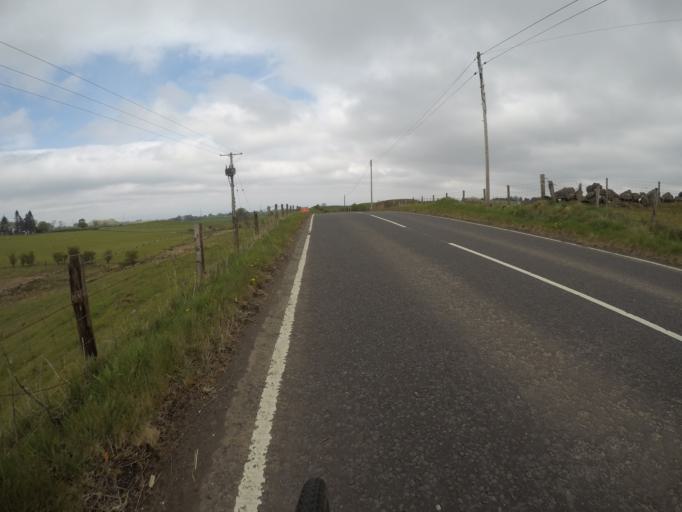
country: GB
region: Scotland
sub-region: East Renfrewshire
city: Barrhead
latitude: 55.7542
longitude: -4.3847
